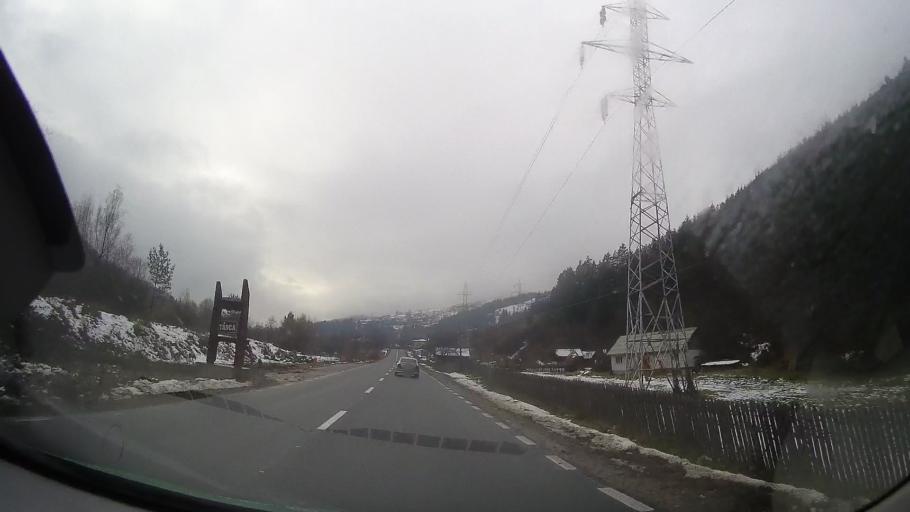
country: RO
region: Neamt
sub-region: Comuna Bicazu Ardelean
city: Bicazu Ardelean
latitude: 46.8696
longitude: 25.9472
